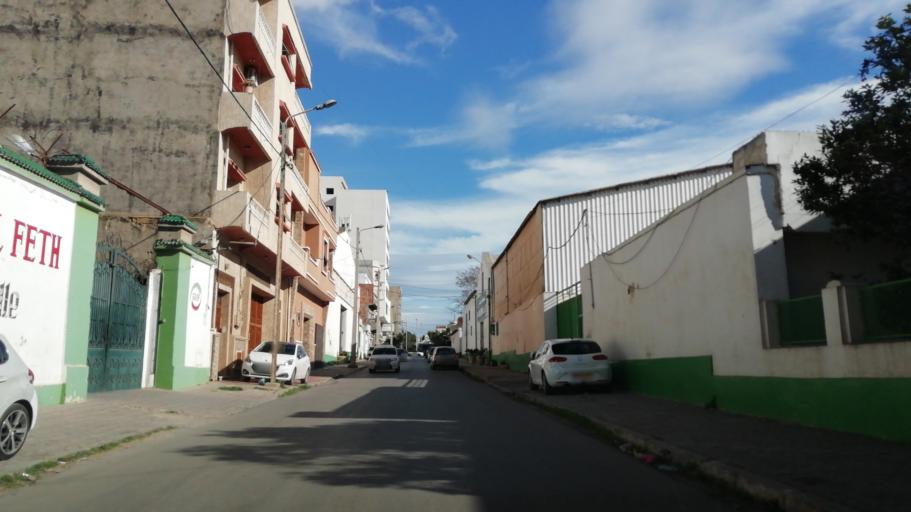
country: DZ
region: Oran
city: Oran
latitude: 35.7003
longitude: -0.6198
